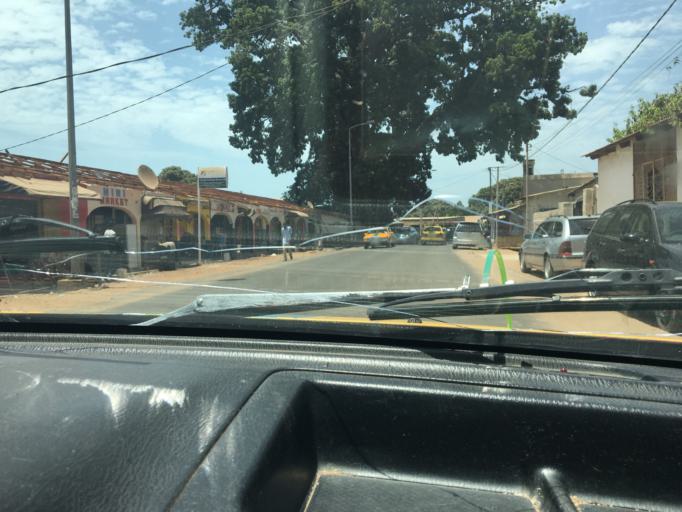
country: GM
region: Banjul
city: Bakau
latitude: 13.4485
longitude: -16.6845
